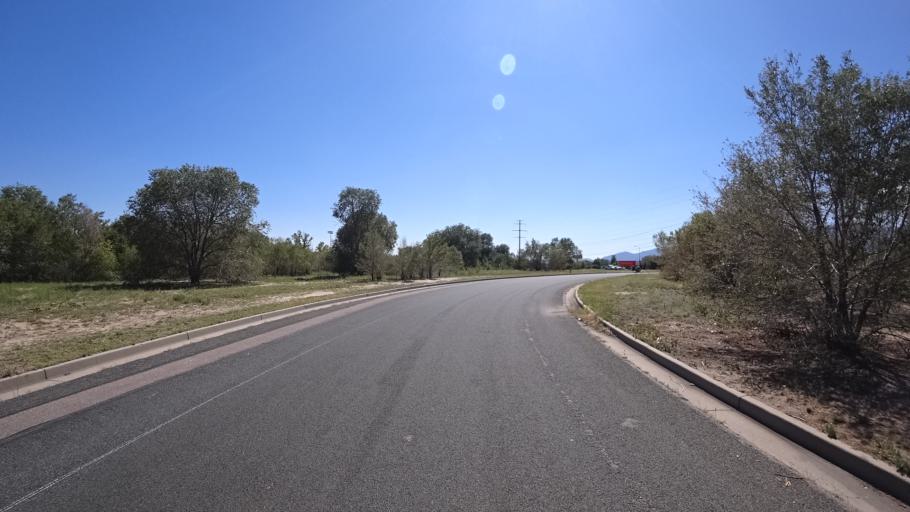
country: US
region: Colorado
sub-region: El Paso County
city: Stratmoor
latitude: 38.8027
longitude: -104.7567
